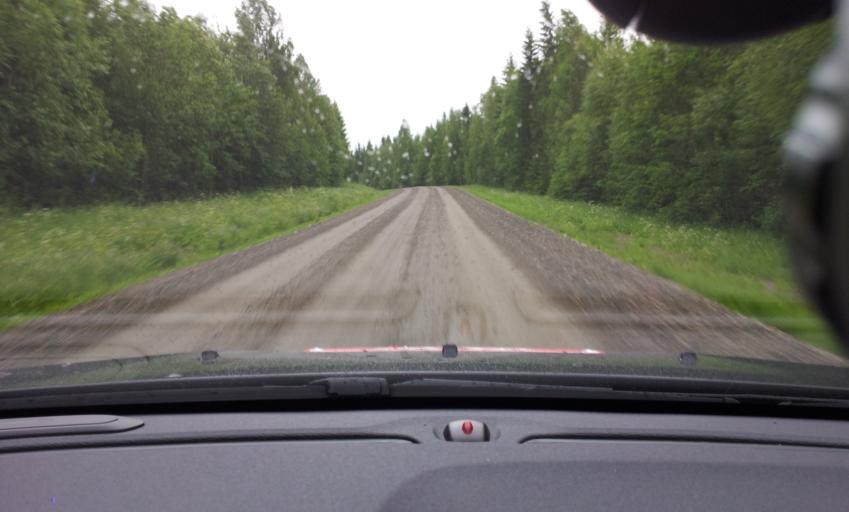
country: SE
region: Jaemtland
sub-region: Ragunda Kommun
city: Hammarstrand
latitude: 63.1253
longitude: 16.3275
